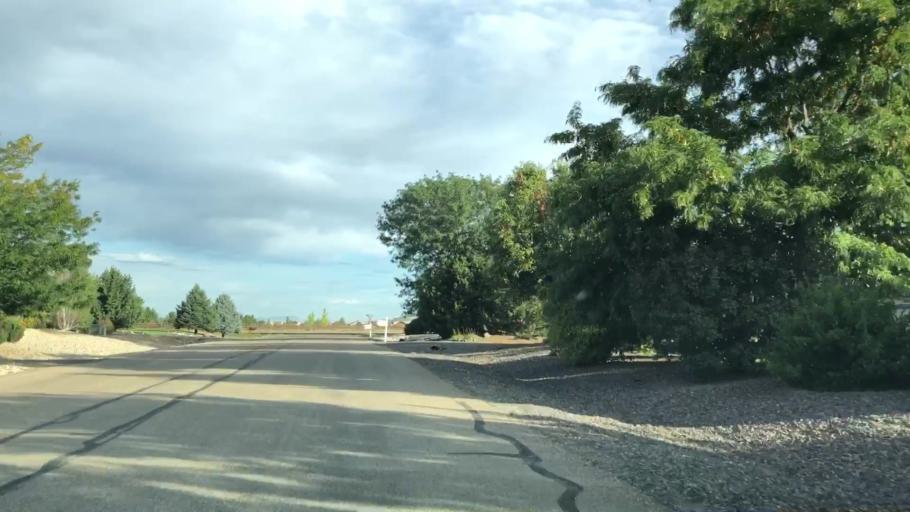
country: US
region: Colorado
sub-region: Weld County
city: Windsor
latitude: 40.4429
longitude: -104.9531
